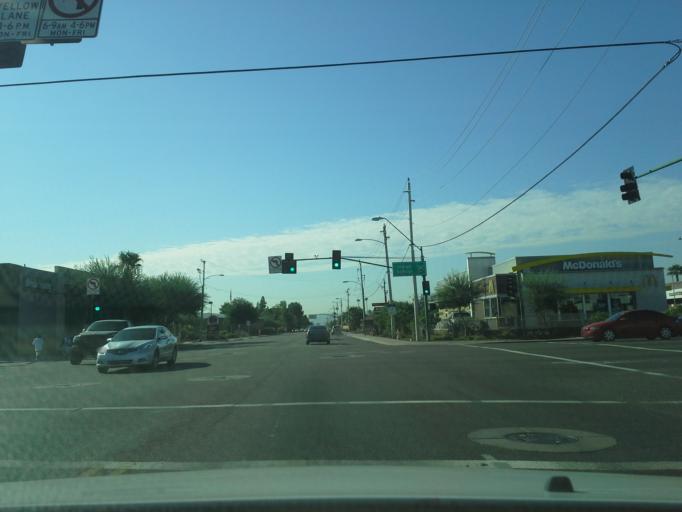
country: US
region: Arizona
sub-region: Maricopa County
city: Phoenix
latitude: 33.4952
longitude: -112.0835
